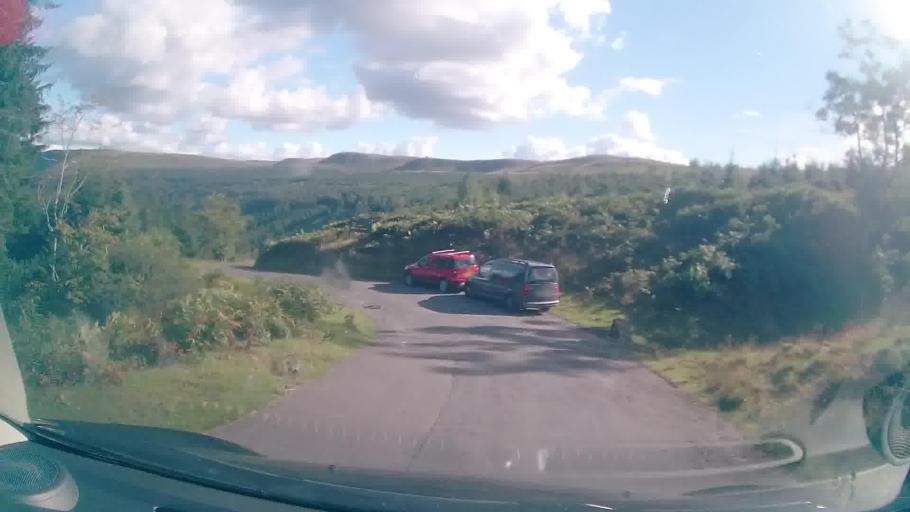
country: GB
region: Wales
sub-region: Sir Powys
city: Brecon
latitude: 51.8482
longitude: -3.3720
